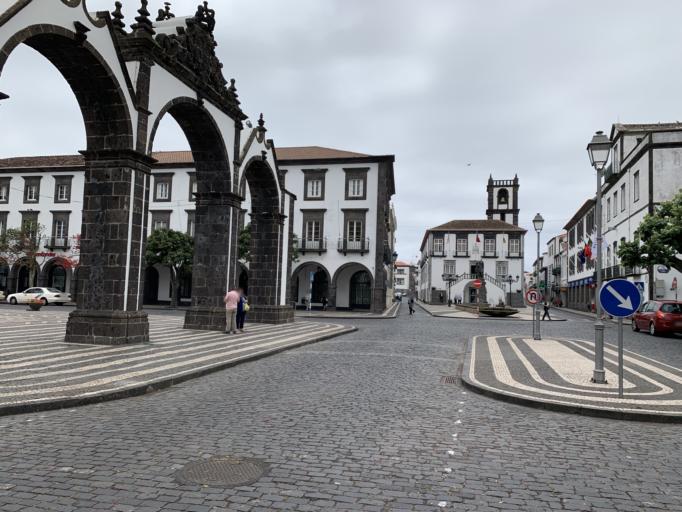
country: PT
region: Azores
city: Ponta Delgada
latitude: 37.7397
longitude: -25.6684
